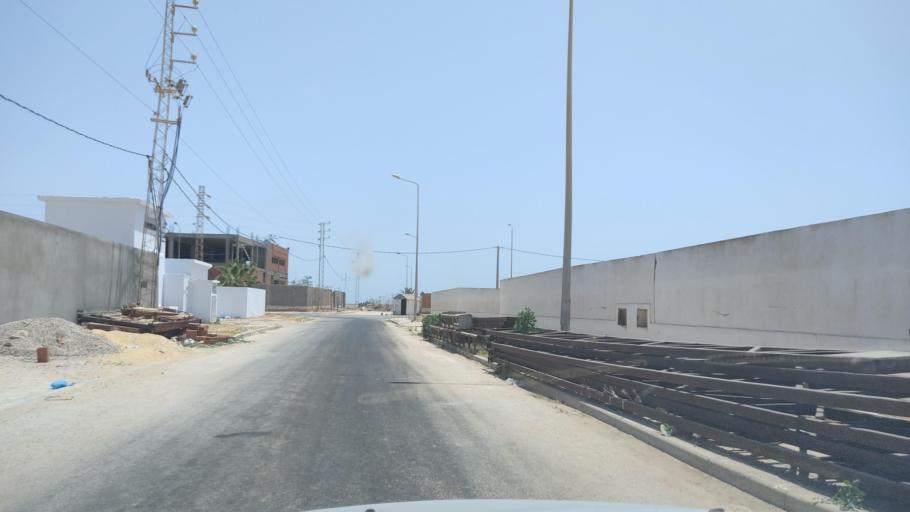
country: TN
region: Safaqis
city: Sfax
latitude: 34.6609
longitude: 10.6990
